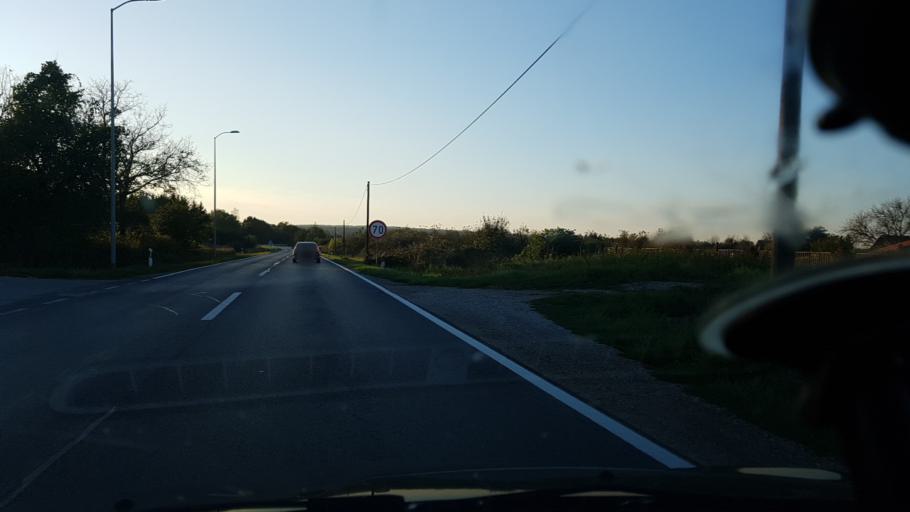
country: HR
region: Koprivnicko-Krizevacka
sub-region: Grad Koprivnica
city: Koprivnica
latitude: 46.1445
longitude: 16.8270
